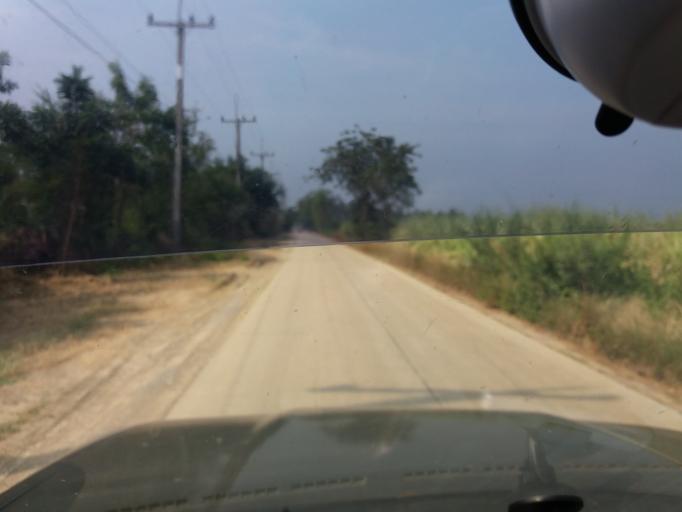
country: TH
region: Suphan Buri
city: Doem Bang Nang Buat
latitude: 14.8934
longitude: 100.1941
